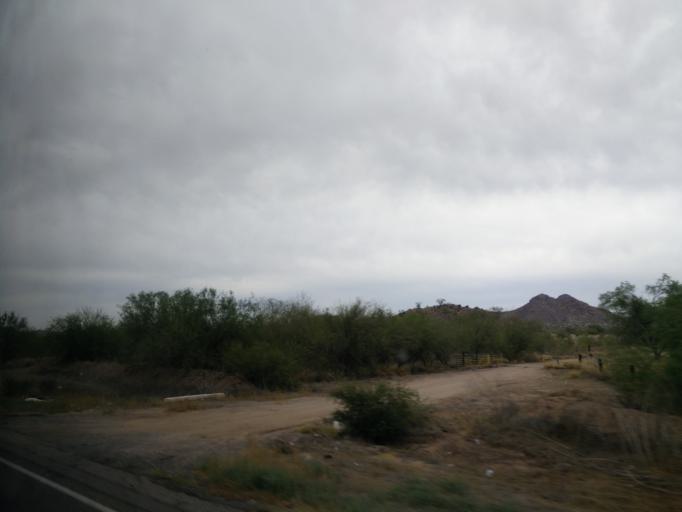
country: MX
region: Sonora
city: Hermosillo
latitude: 28.8762
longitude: -110.9584
